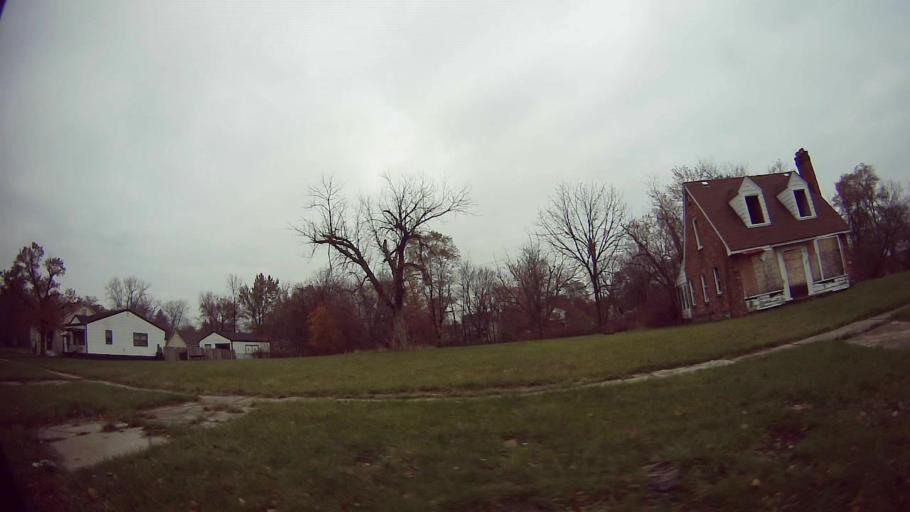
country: US
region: Michigan
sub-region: Wayne County
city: Redford
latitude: 42.4046
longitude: -83.2569
